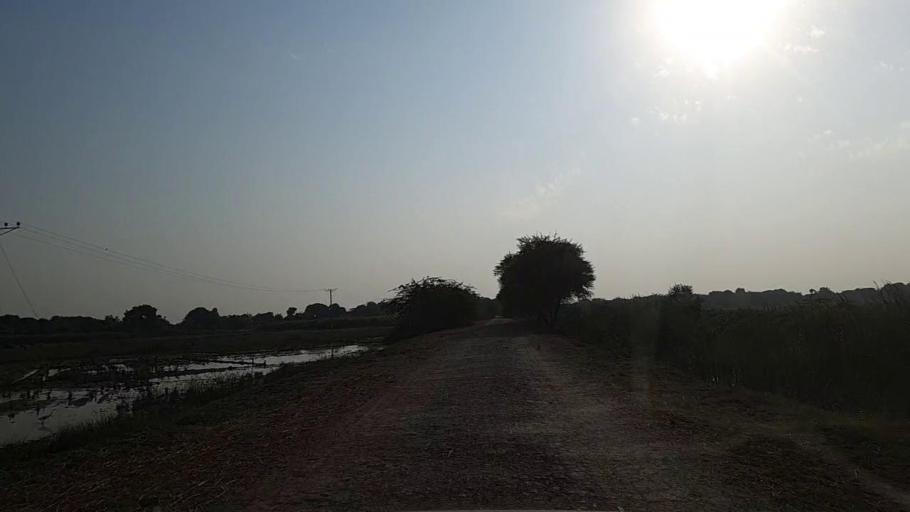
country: PK
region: Sindh
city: Mirpur Batoro
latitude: 24.7862
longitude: 68.2479
